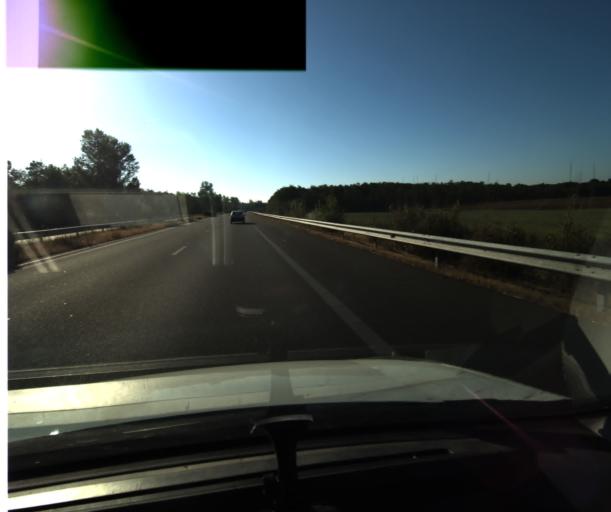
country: FR
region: Midi-Pyrenees
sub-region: Departement du Tarn-et-Garonne
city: Saint-Porquier
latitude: 44.0144
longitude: 1.2013
